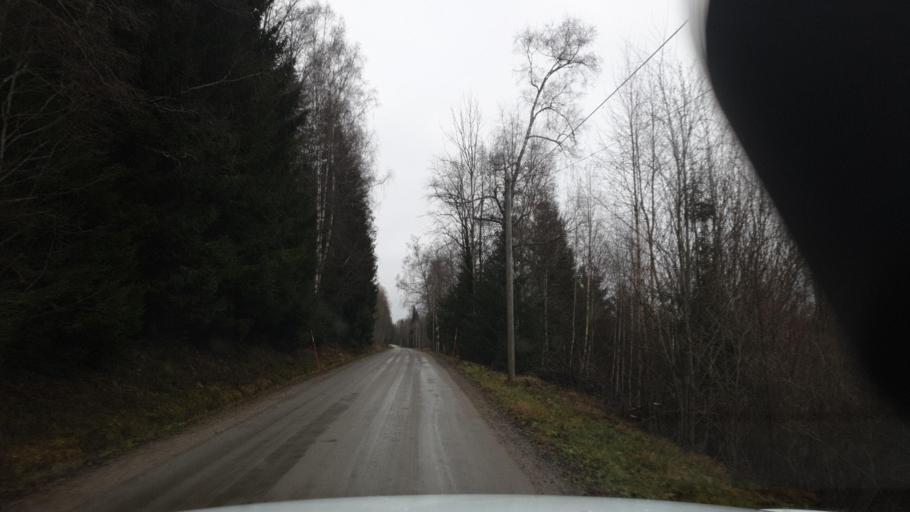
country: SE
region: Vaermland
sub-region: Eda Kommun
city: Amotfors
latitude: 59.7401
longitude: 12.2776
